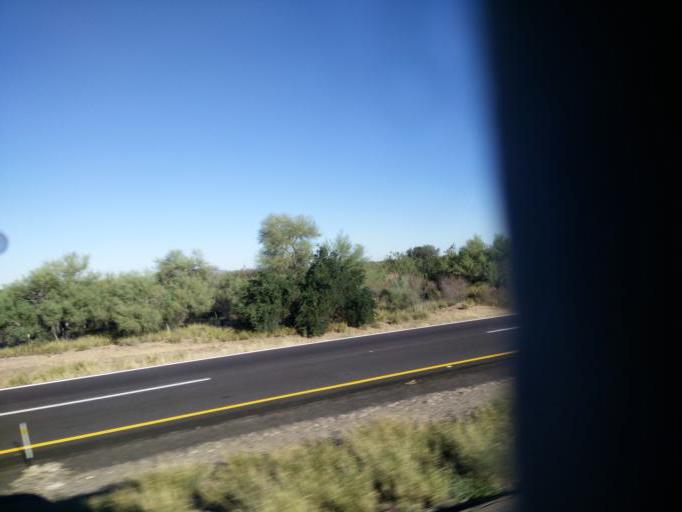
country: MX
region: Sonora
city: Hermosillo
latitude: 28.6599
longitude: -111.0022
